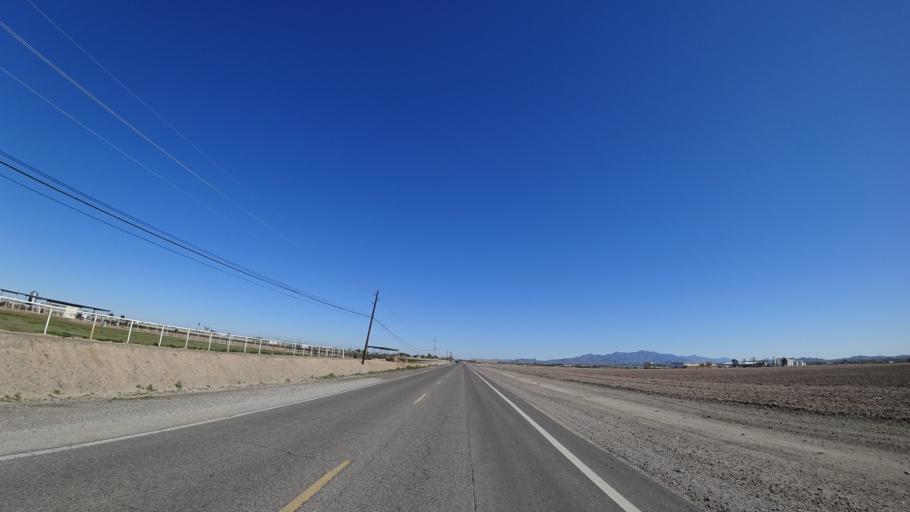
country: US
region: Arizona
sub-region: Maricopa County
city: Buckeye
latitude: 33.3923
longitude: -112.5429
